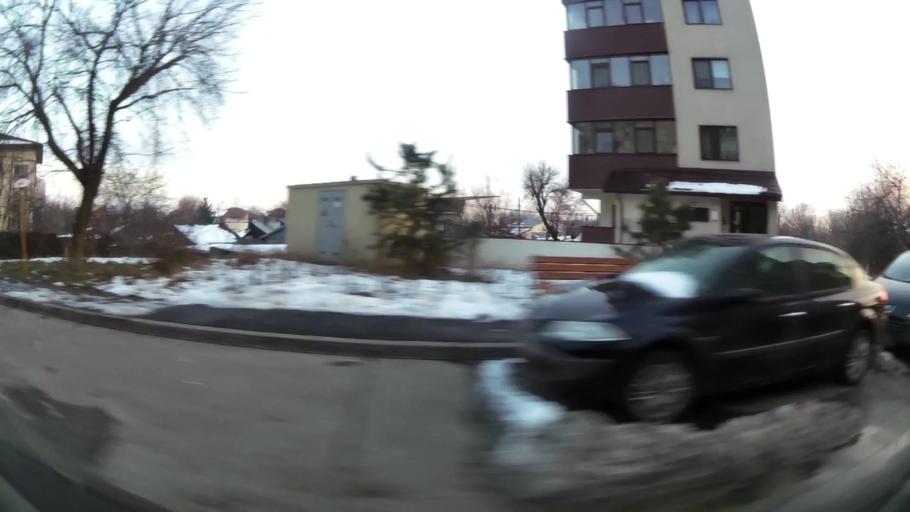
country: RO
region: Ilfov
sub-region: Comuna Fundeni-Dobroesti
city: Fundeni
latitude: 44.4632
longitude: 26.1464
